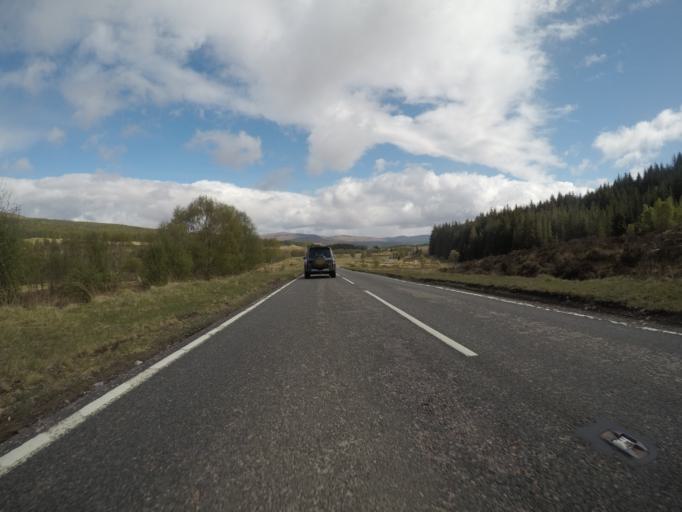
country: GB
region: Scotland
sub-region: Highland
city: Spean Bridge
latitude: 57.1267
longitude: -4.9651
